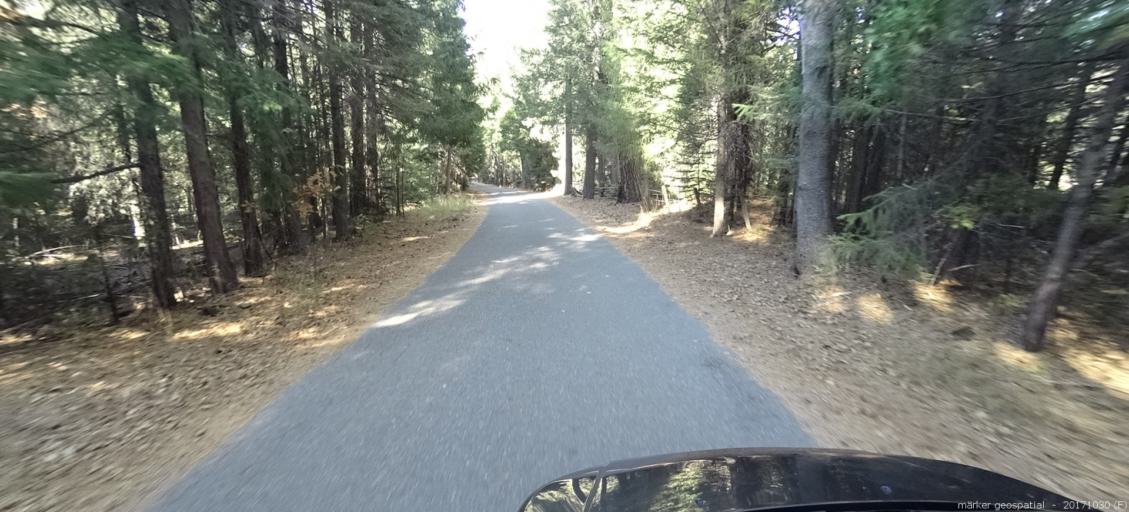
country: US
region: California
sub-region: Shasta County
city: Shingletown
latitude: 40.5262
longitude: -121.6889
